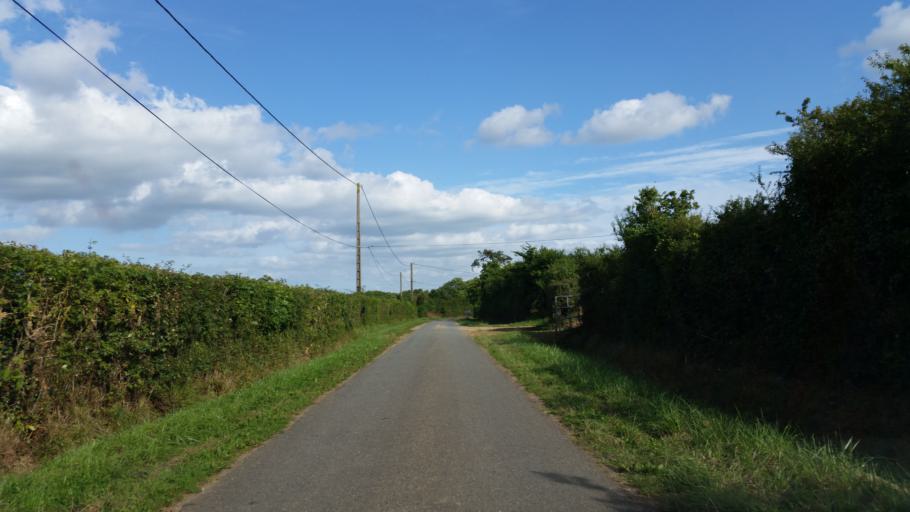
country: FR
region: Lower Normandy
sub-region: Departement de la Manche
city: Sainte-Mere-Eglise
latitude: 49.4580
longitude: -1.2943
